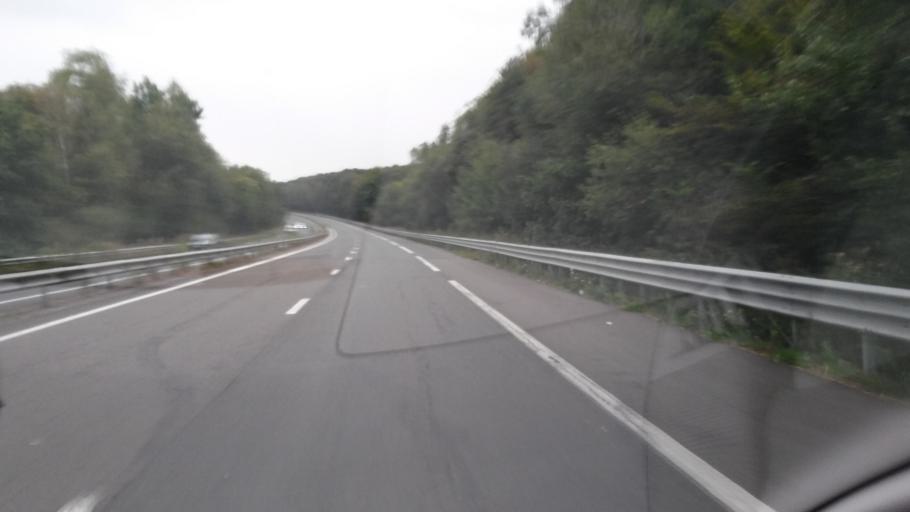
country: FR
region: Champagne-Ardenne
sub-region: Departement des Ardennes
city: Douzy
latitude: 49.7362
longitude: 5.0194
